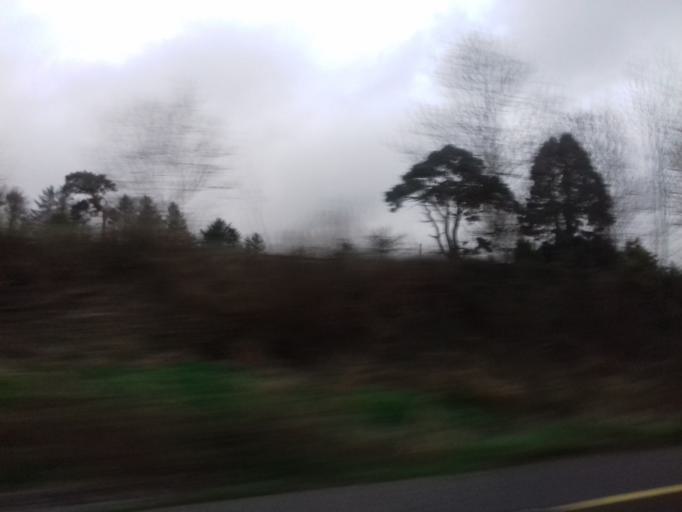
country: IE
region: Munster
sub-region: Ciarrai
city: Castleisland
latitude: 52.3012
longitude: -9.3827
